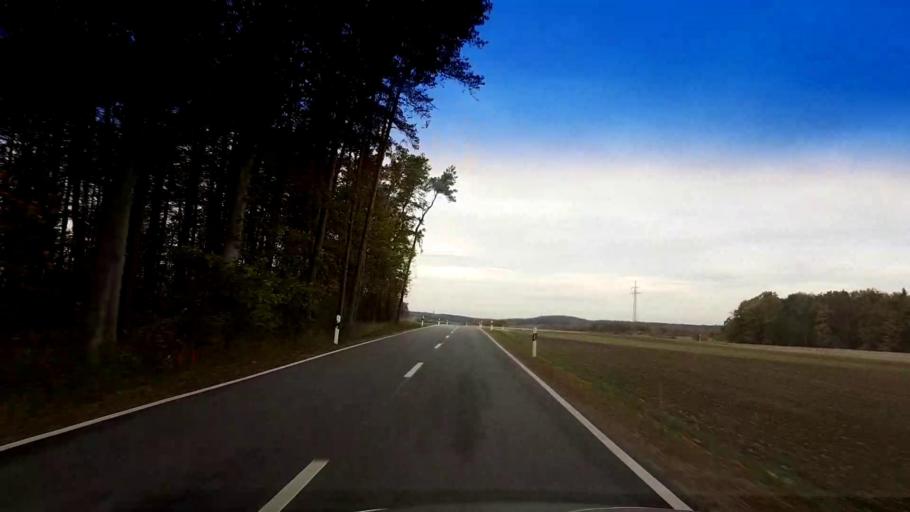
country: DE
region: Bavaria
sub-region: Upper Franconia
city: Priesendorf
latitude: 49.9247
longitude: 10.7091
